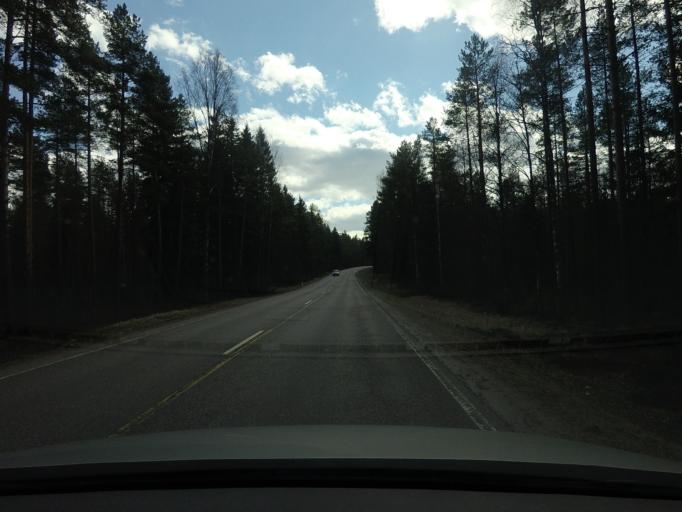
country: FI
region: Kymenlaakso
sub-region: Kotka-Hamina
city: Hamina
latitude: 60.7636
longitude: 27.3483
